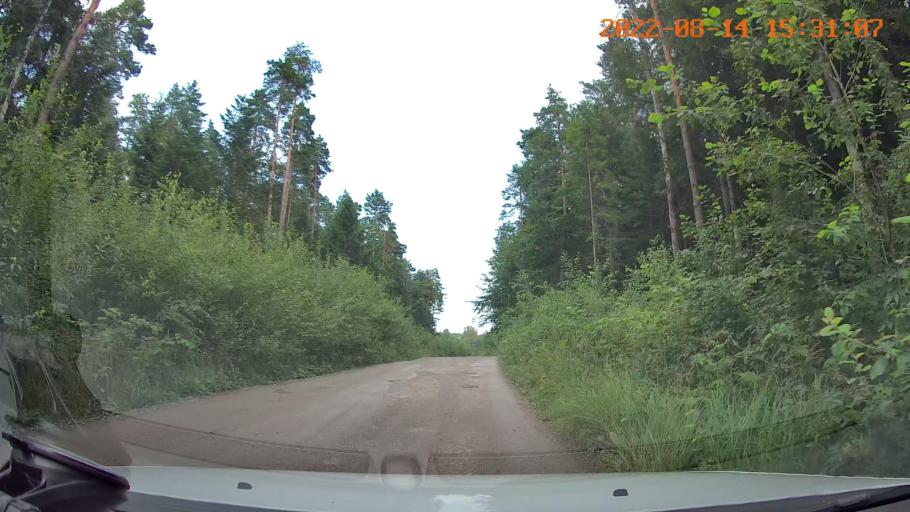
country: PL
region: Swietokrzyskie
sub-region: Powiat kielecki
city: Zagnansk
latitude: 50.9671
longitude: 20.6617
